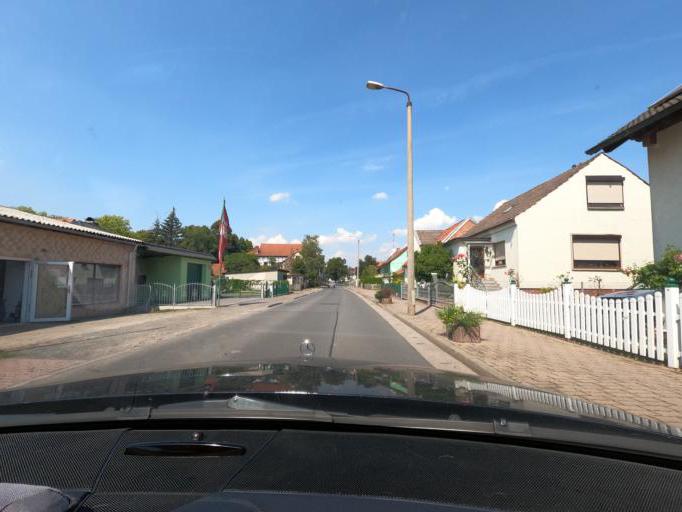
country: DE
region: Thuringia
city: Nordhausen
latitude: 51.5145
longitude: 10.7705
